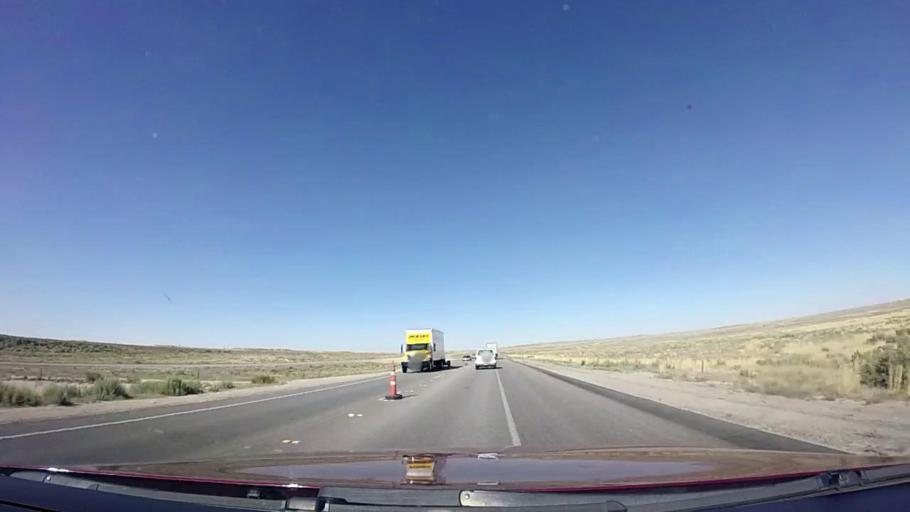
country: US
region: Wyoming
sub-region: Carbon County
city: Rawlins
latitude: 41.7062
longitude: -107.8779
